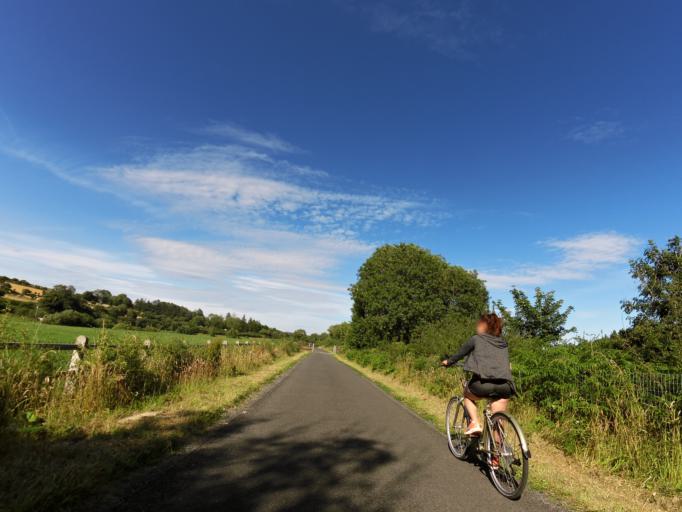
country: IE
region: Munster
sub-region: Waterford
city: Portlaw
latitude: 52.2316
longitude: -7.3100
